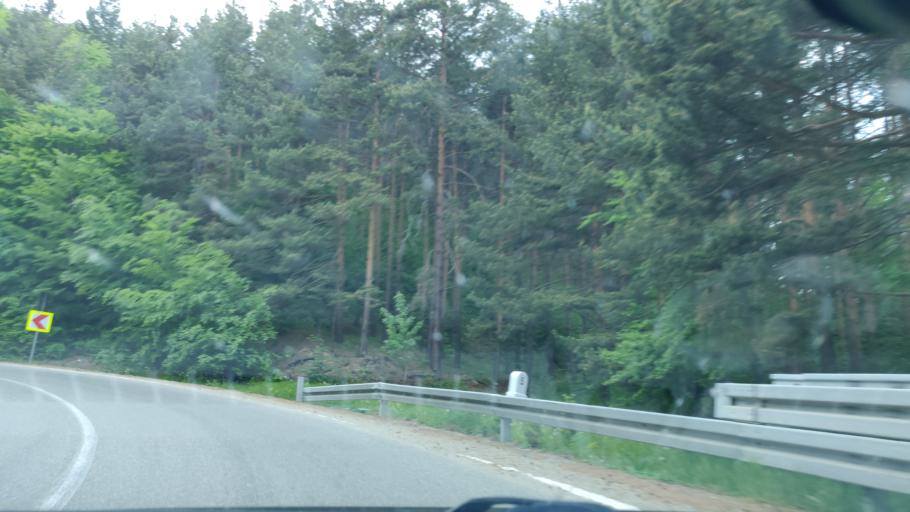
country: RO
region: Vrancea
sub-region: Comuna Tulnici
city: Tulnici
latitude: 45.9201
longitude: 26.6631
